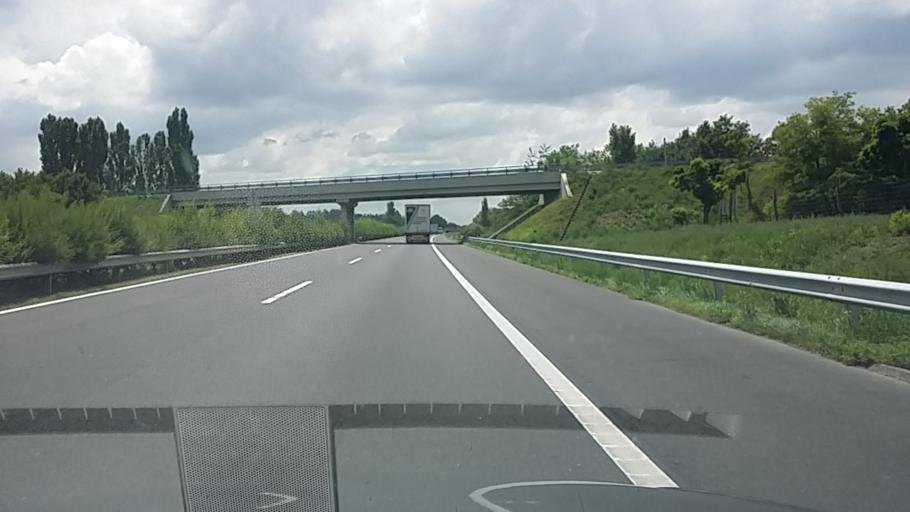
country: HU
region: Bacs-Kiskun
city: Kecskemet
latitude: 46.9521
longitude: 19.6201
